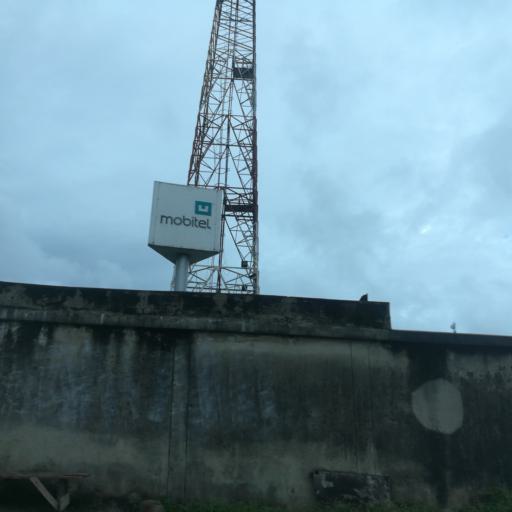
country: NG
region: Lagos
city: Ikoyi
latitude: 6.4390
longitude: 3.4685
